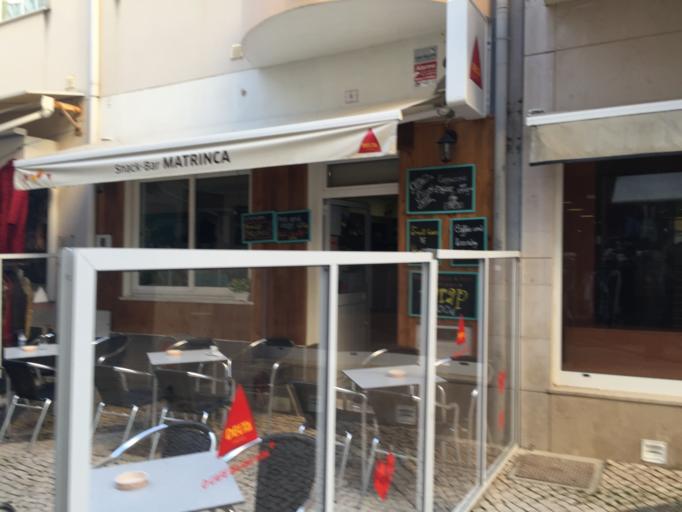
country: PT
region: Faro
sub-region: Vila Real de Santo Antonio
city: Monte Gordo
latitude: 37.1817
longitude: -7.4519
